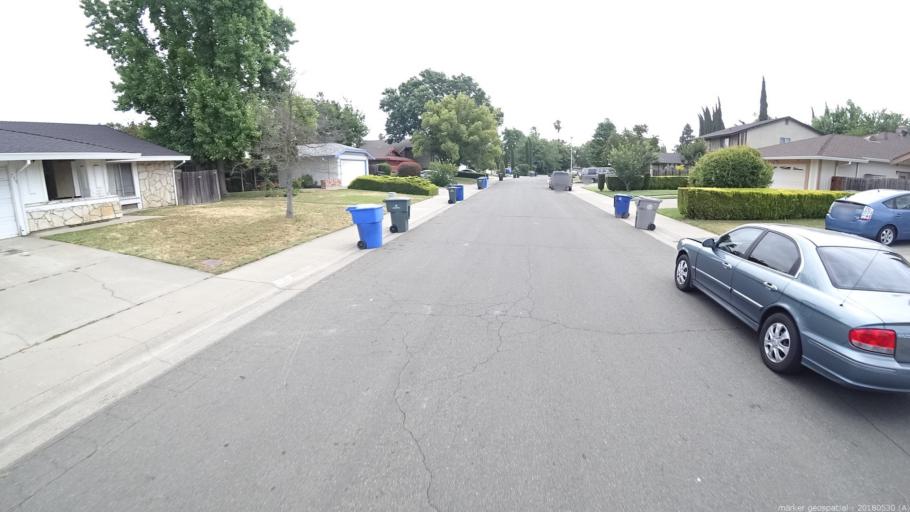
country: US
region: California
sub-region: Sacramento County
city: Sacramento
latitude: 38.6199
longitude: -121.4787
